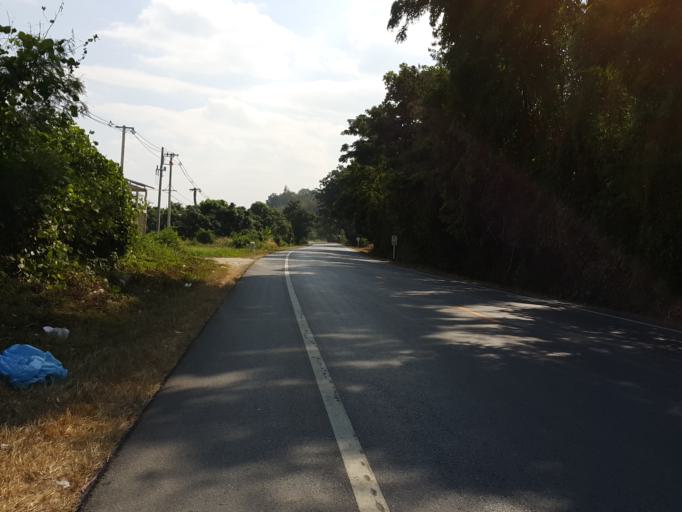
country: TH
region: Lamphun
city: Ban Hong
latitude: 18.2852
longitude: 98.8176
